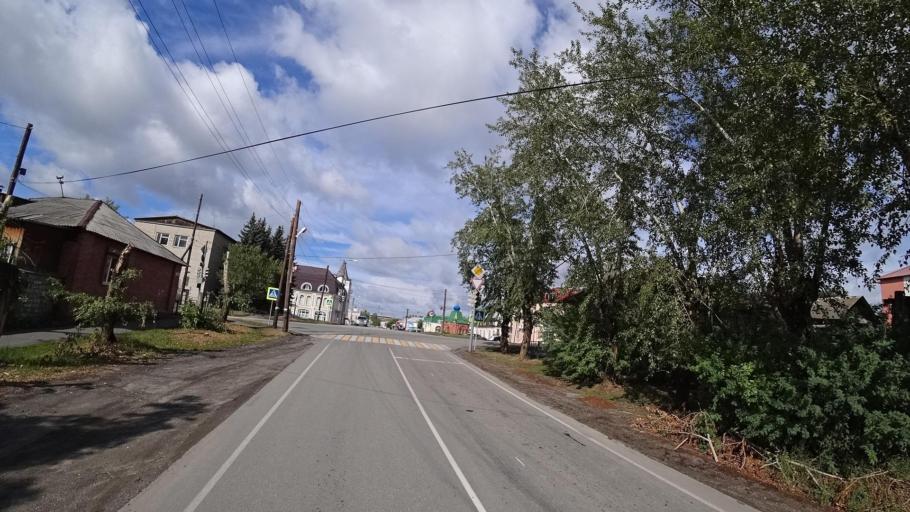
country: RU
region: Sverdlovsk
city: Kamyshlov
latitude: 56.8424
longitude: 62.7063
